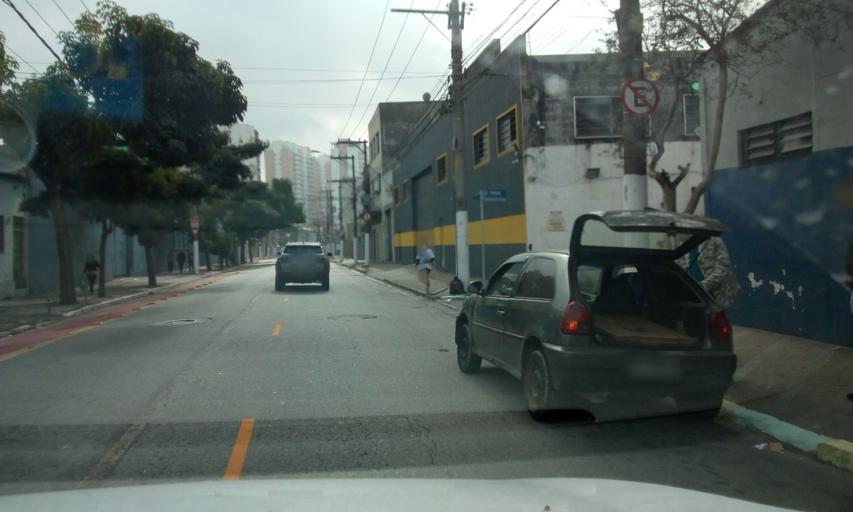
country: BR
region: Sao Paulo
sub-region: Sao Paulo
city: Sao Paulo
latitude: -23.5284
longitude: -46.6042
